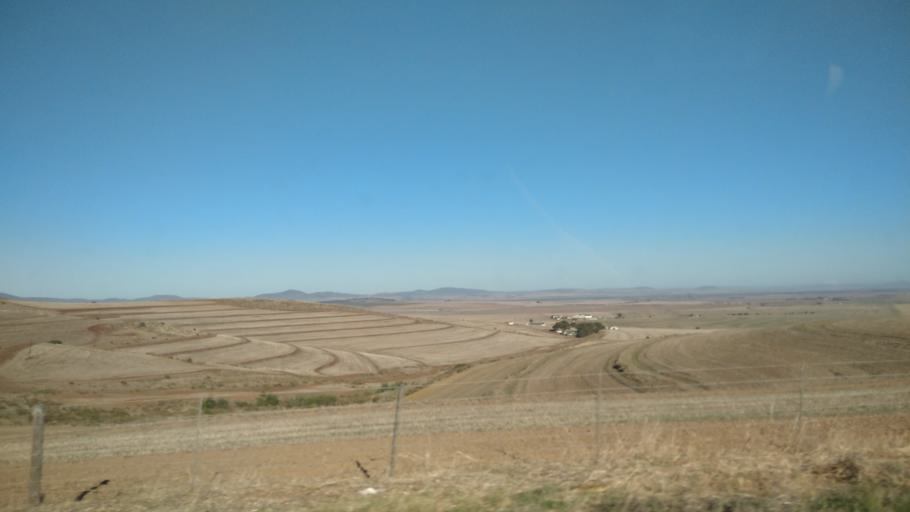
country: ZA
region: Western Cape
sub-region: West Coast District Municipality
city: Malmesbury
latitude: -33.3882
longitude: 18.6713
